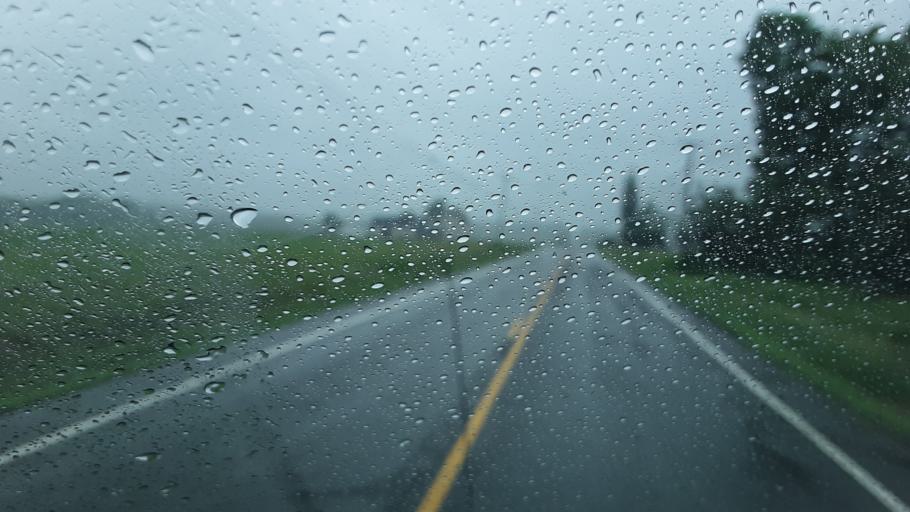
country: US
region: Maine
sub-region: Penobscot County
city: Patten
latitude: 46.0153
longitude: -68.4459
